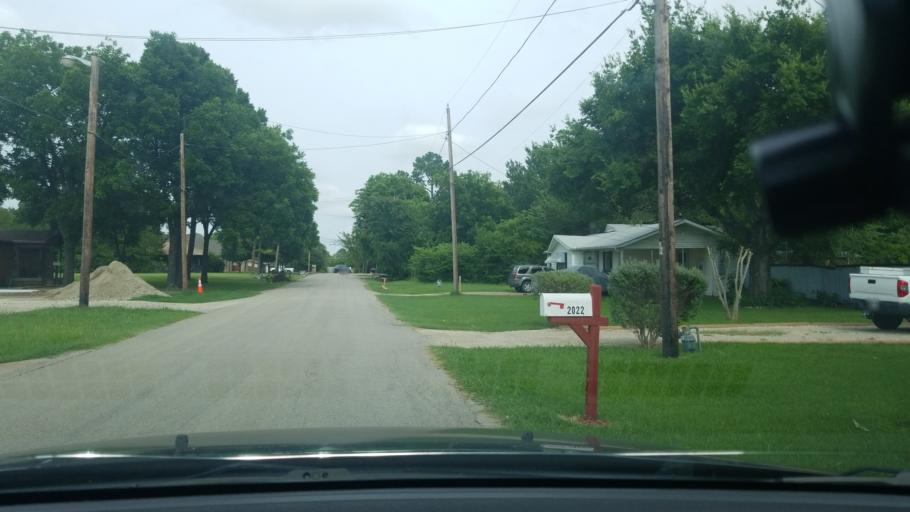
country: US
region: Texas
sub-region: Dallas County
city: Balch Springs
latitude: 32.7548
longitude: -96.6298
